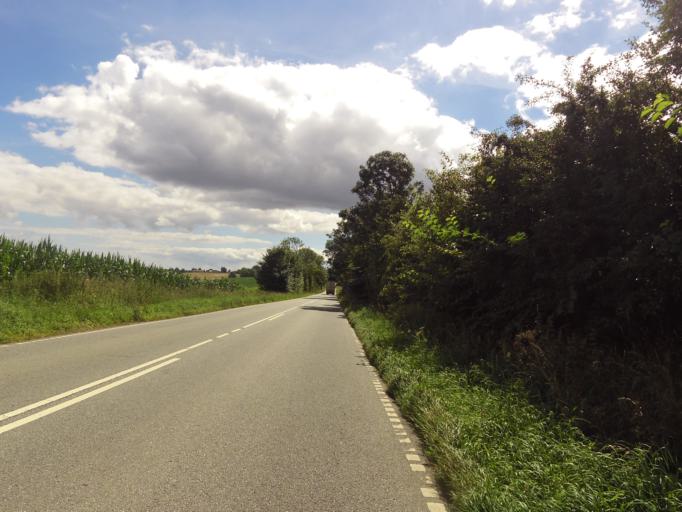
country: DK
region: South Denmark
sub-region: Haderslev Kommune
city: Haderslev
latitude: 55.2614
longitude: 9.4406
